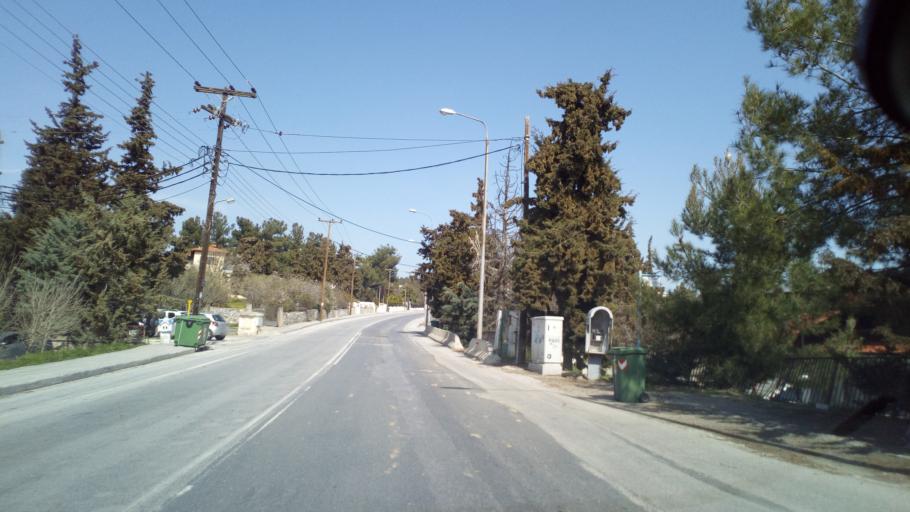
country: GR
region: Central Macedonia
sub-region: Nomos Thessalonikis
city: Panorama
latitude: 40.5928
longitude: 23.0454
